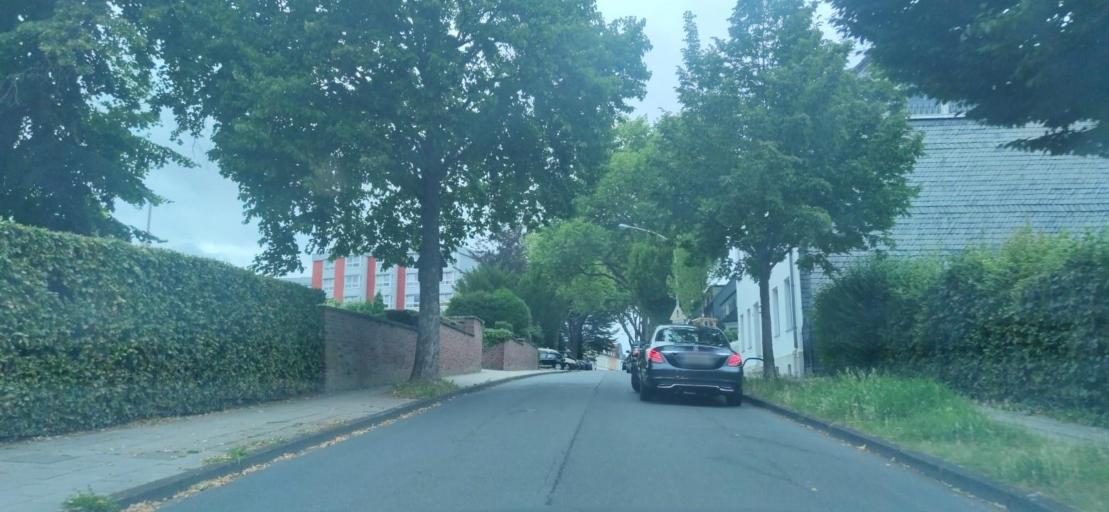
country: DE
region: North Rhine-Westphalia
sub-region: Regierungsbezirk Dusseldorf
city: Essen
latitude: 51.4267
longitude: 7.0776
